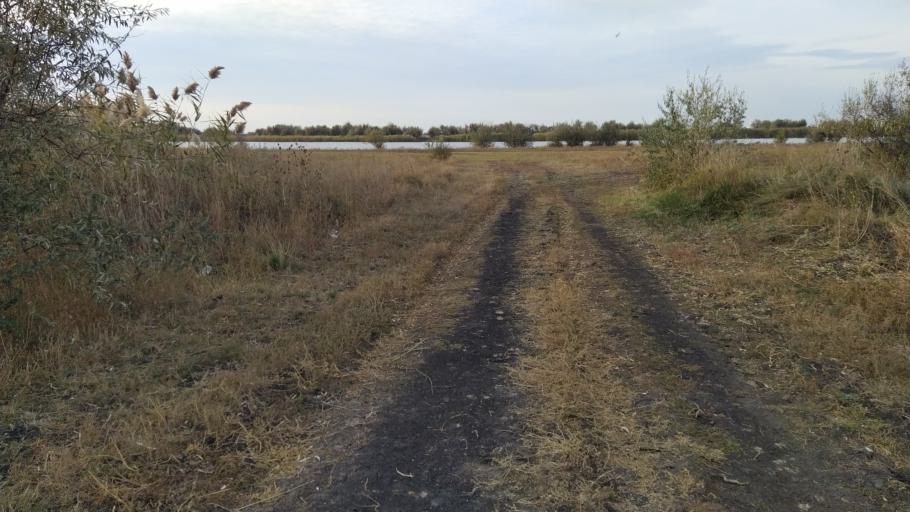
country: RU
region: Rostov
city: Kuleshovka
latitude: 47.1215
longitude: 39.6294
